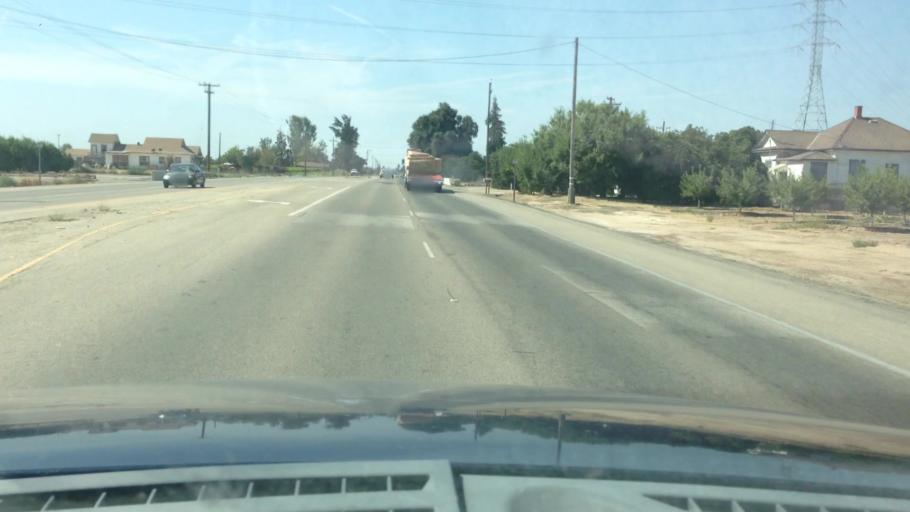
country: US
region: California
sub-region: Fresno County
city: Del Rey
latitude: 36.6425
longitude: -119.5565
